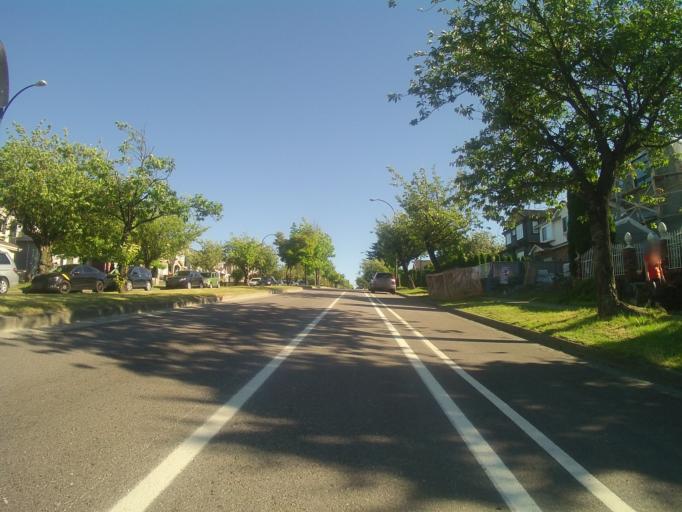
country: CA
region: British Columbia
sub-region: Fraser Valley Regional District
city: North Vancouver
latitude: 49.2545
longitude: -123.0339
